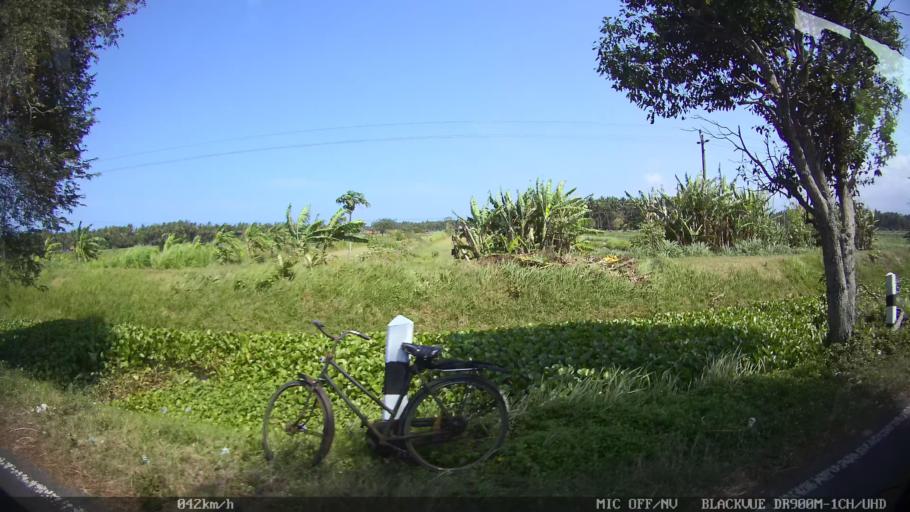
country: ID
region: Daerah Istimewa Yogyakarta
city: Srandakan
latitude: -7.9338
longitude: 110.1555
